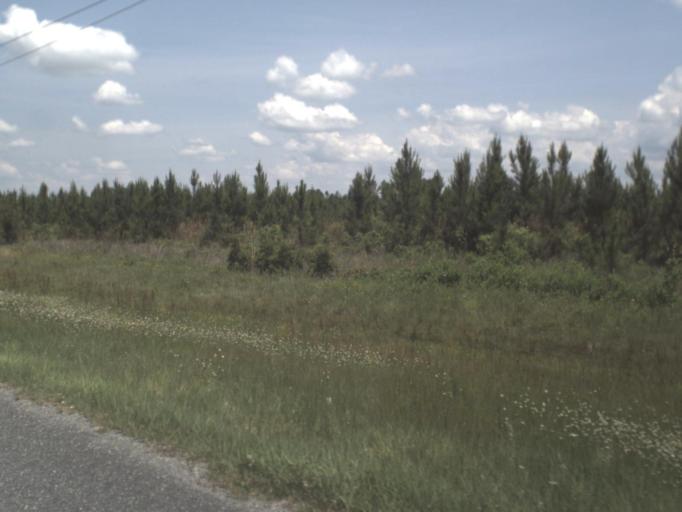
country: US
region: Florida
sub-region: Bradford County
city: Starke
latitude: 29.9706
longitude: -82.2083
